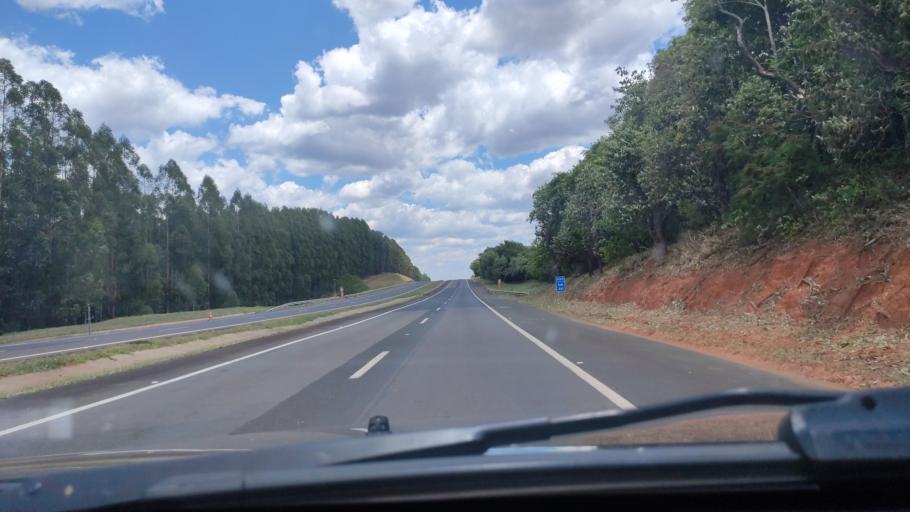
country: BR
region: Sao Paulo
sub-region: Duartina
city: Duartina
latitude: -22.4885
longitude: -49.2450
